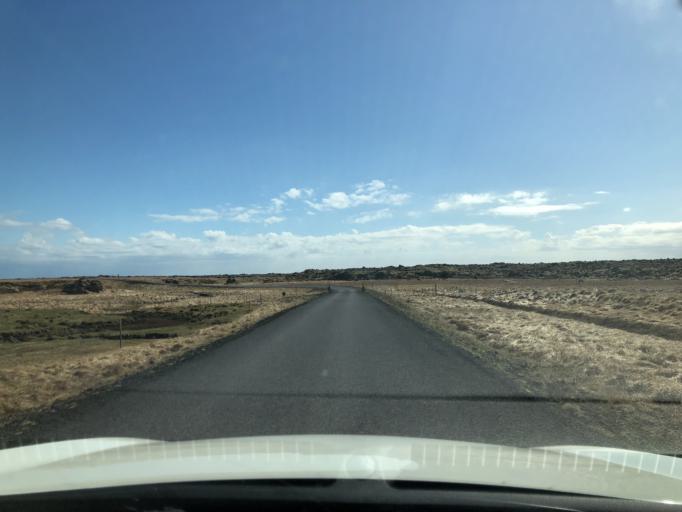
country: IS
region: West
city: Olafsvik
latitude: 64.8297
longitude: -23.4053
